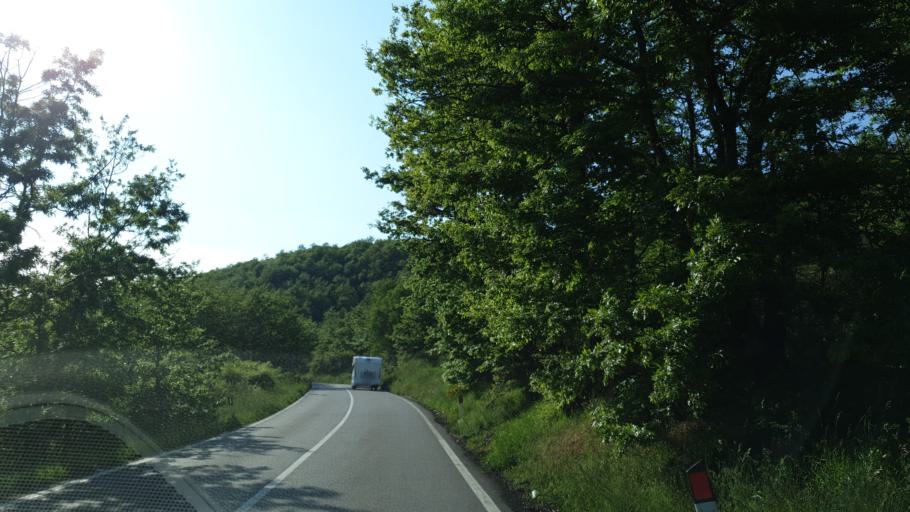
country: IT
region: Tuscany
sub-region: Province of Arezzo
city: Stia
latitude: 43.7808
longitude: 11.6722
